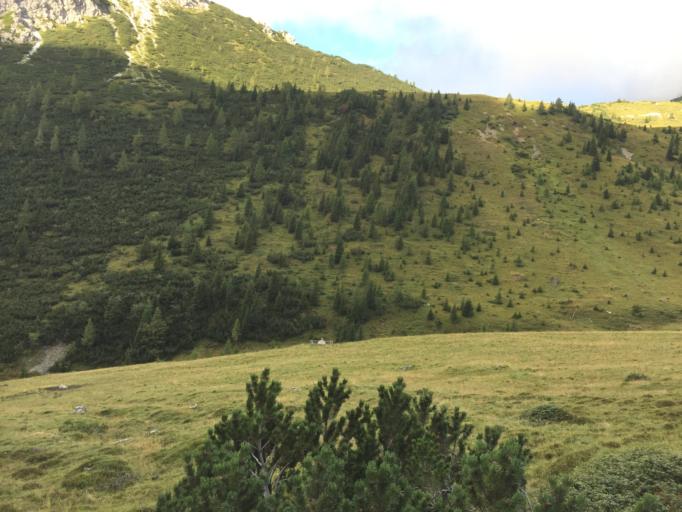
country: IT
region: Veneto
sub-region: Provincia di Belluno
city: San Pietro di Cadore
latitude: 46.6185
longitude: 12.5841
